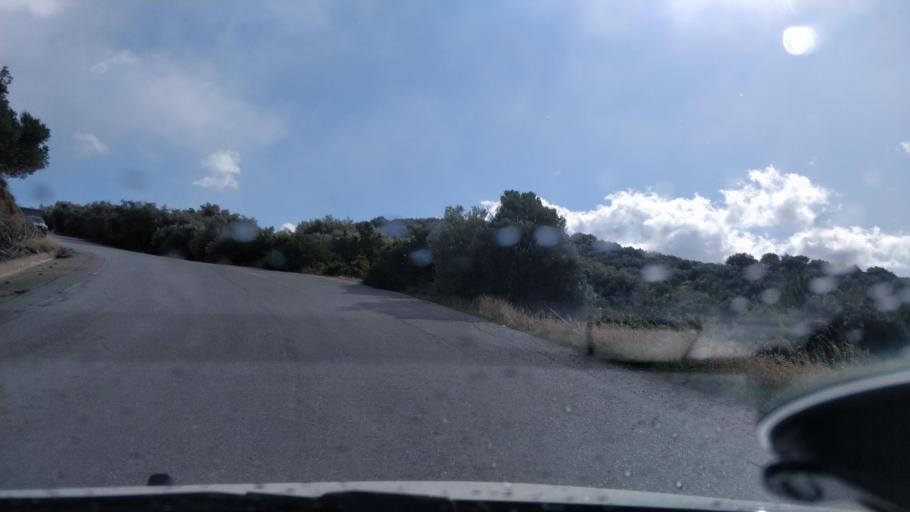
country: GR
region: Crete
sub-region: Nomos Lasithiou
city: Gra Liyia
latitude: 34.9952
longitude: 25.5118
